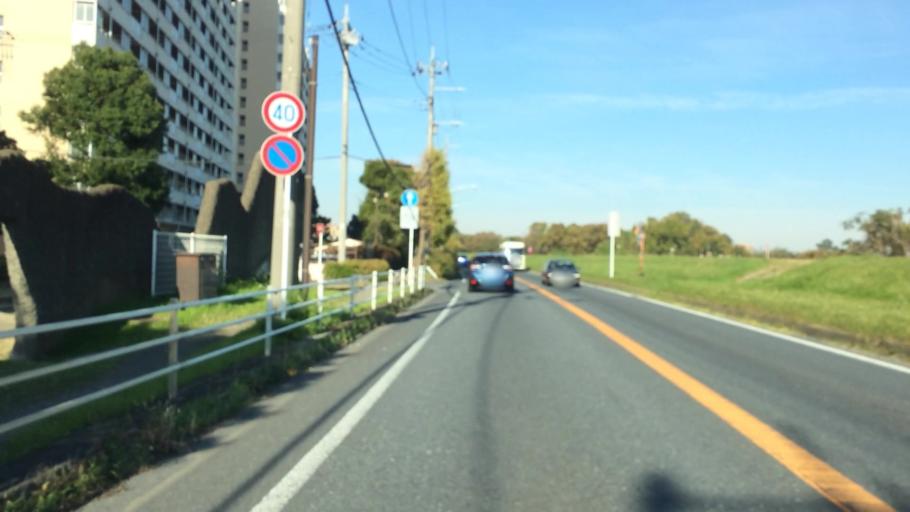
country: JP
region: Tokyo
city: Chofugaoka
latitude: 35.6314
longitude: 139.5617
